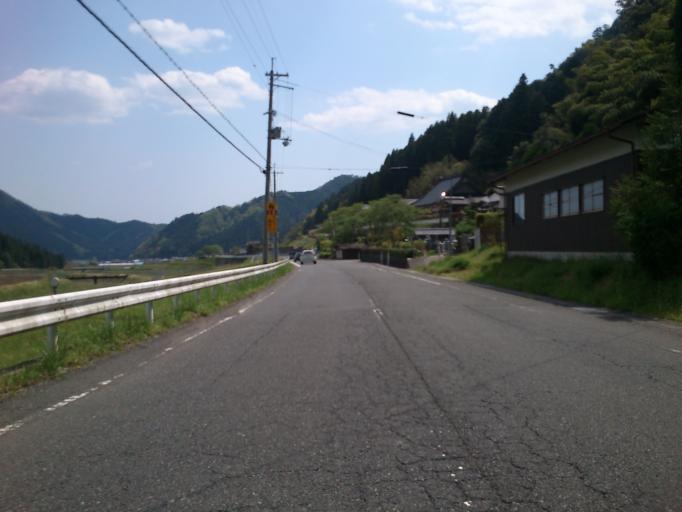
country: JP
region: Kyoto
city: Fukuchiyama
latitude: 35.3643
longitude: 134.9385
